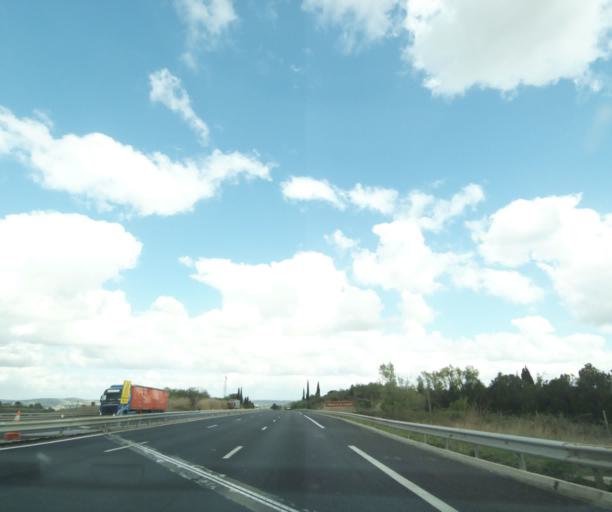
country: FR
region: Languedoc-Roussillon
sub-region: Departement du Gard
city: Sernhac
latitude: 43.9027
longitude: 4.5439
